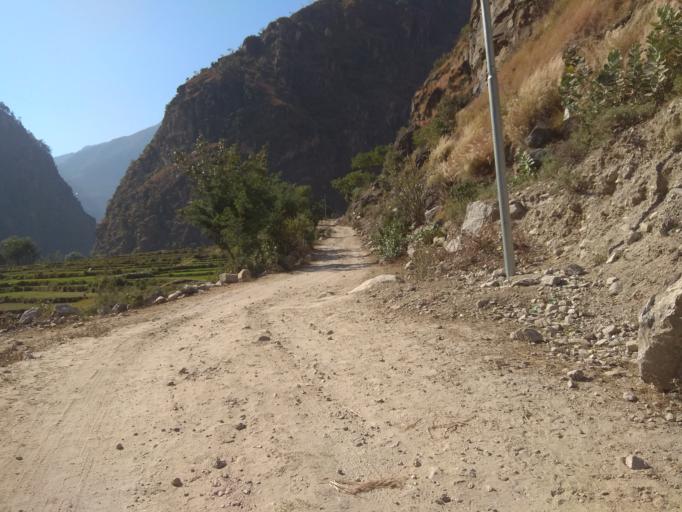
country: NP
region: Far Western
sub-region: Seti Zone
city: Achham
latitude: 29.2195
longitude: 81.6359
